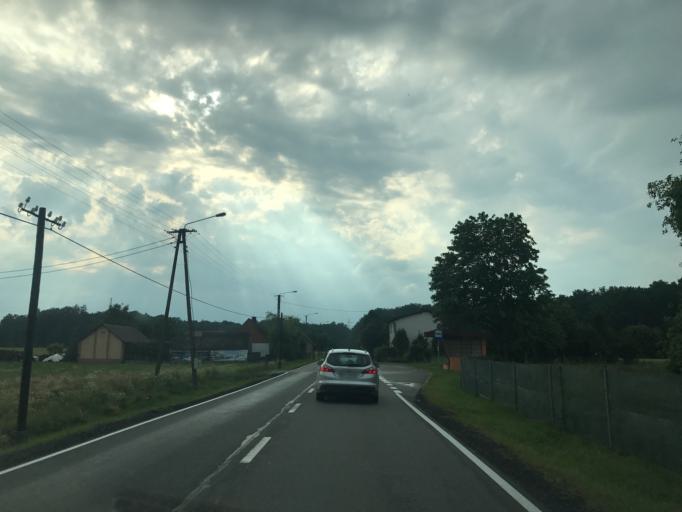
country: PL
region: Pomeranian Voivodeship
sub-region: Powiat czluchowski
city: Czluchow
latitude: 53.6899
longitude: 17.3101
